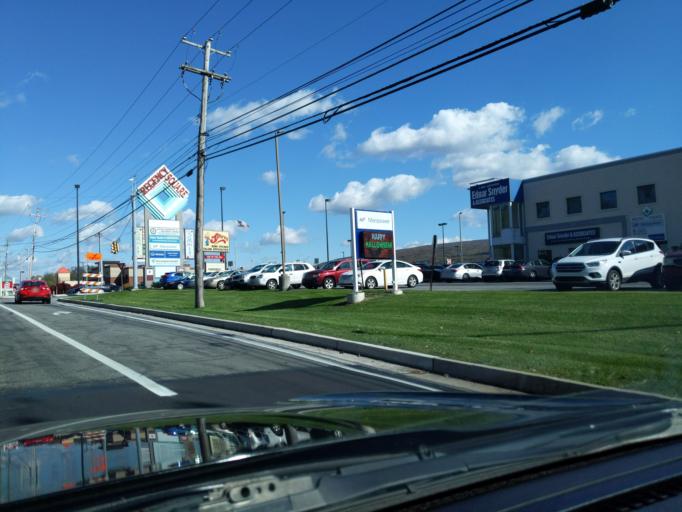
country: US
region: Pennsylvania
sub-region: Blair County
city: Lakemont
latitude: 40.4581
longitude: -78.4094
